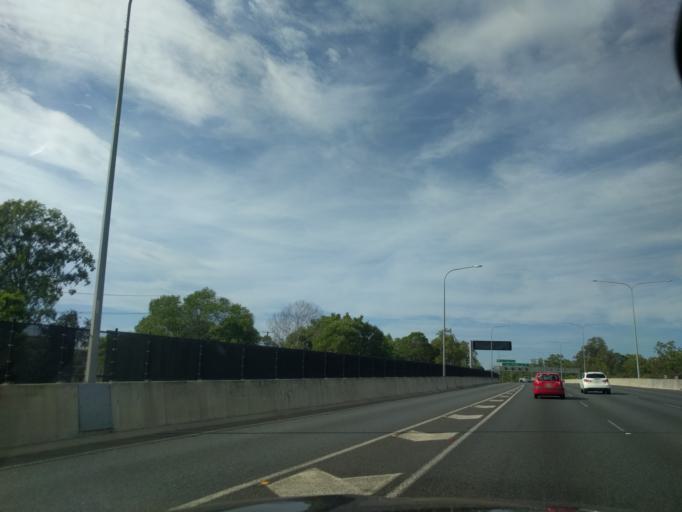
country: AU
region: Queensland
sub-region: Brisbane
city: Wacol
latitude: -27.5927
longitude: 152.9243
